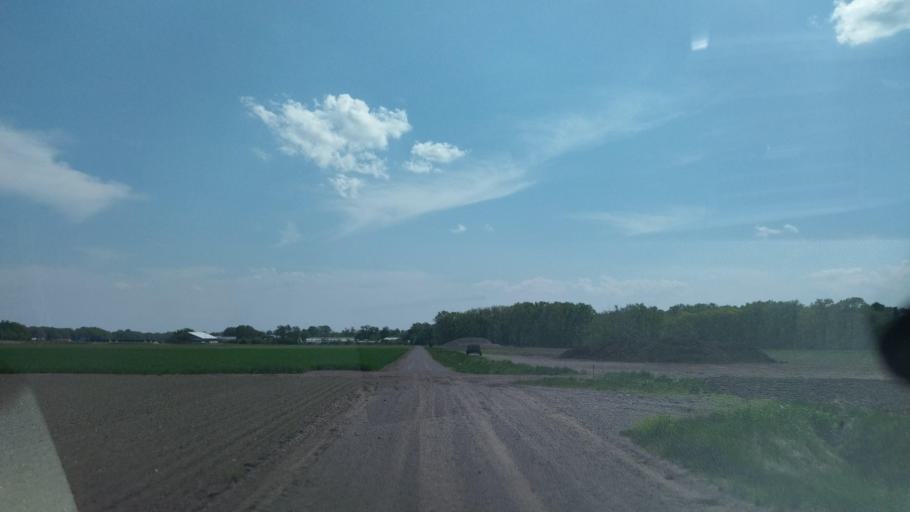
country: JP
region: Hokkaido
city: Otofuke
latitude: 43.1376
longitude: 143.2196
